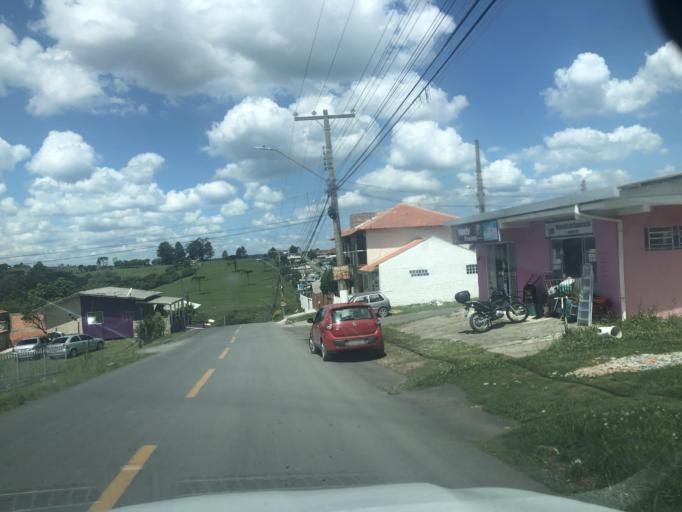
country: BR
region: Santa Catarina
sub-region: Lages
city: Lages
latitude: -27.7859
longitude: -50.3164
